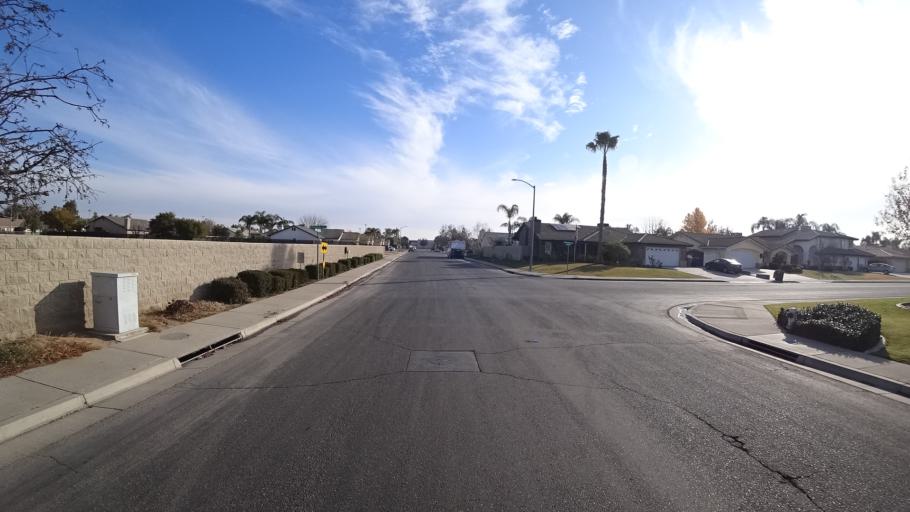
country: US
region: California
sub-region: Kern County
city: Rosedale
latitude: 35.4011
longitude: -119.1396
